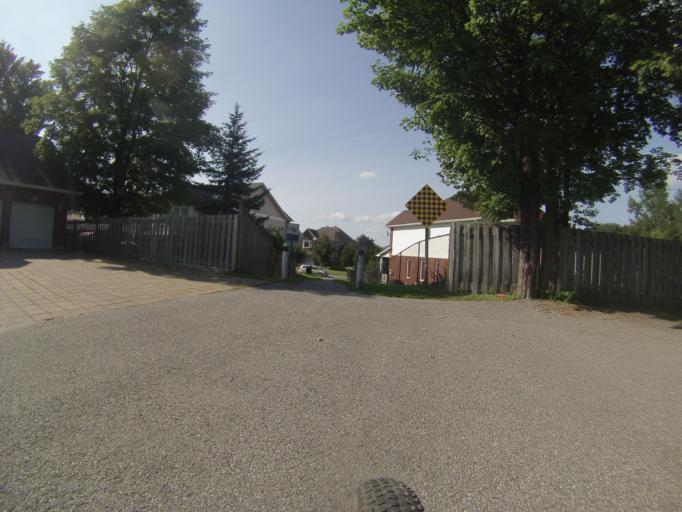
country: CA
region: Ontario
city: Ottawa
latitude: 45.3545
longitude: -75.6288
